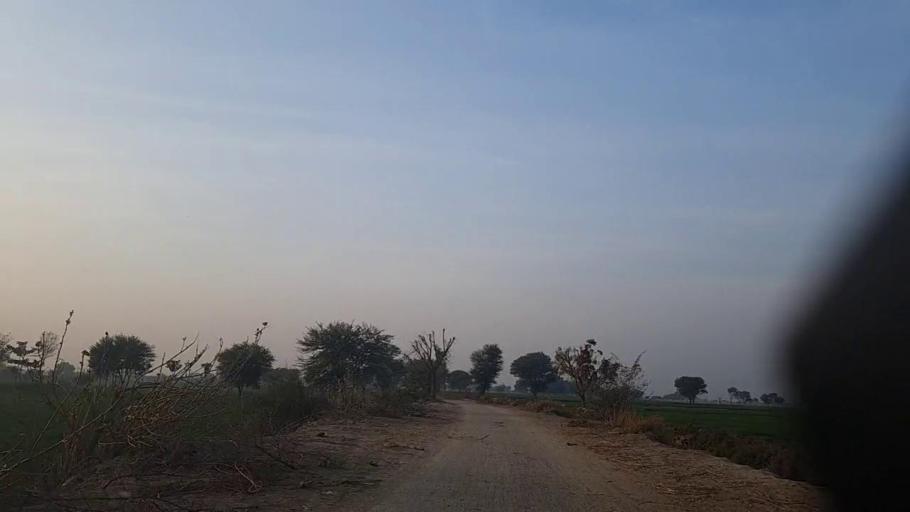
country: PK
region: Sindh
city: Sakrand
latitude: 26.1331
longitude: 68.2284
